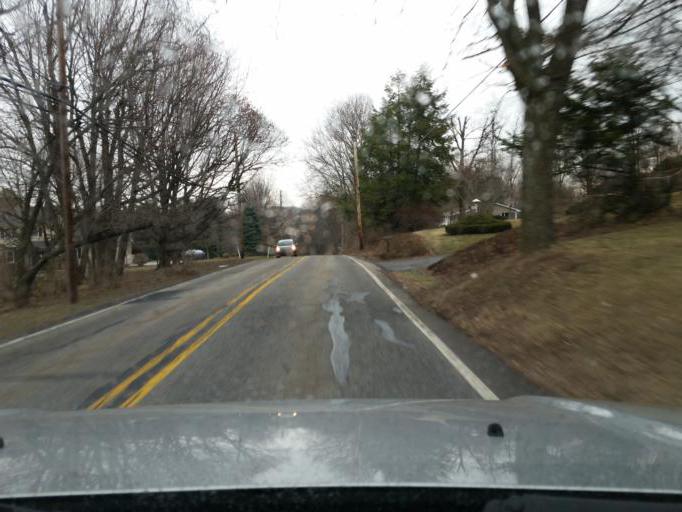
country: US
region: Pennsylvania
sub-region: Dauphin County
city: Paxtonia
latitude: 40.3100
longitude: -76.7759
